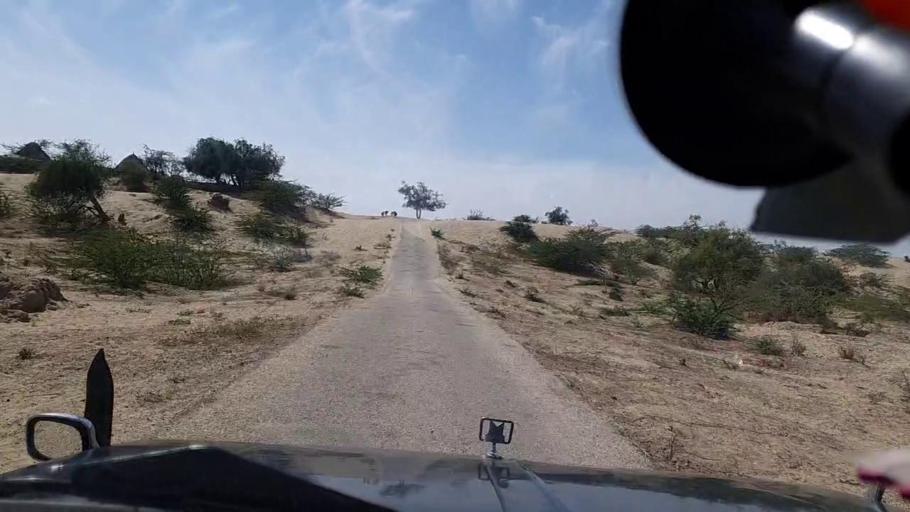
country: PK
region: Sindh
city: Diplo
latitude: 24.3713
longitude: 69.5838
